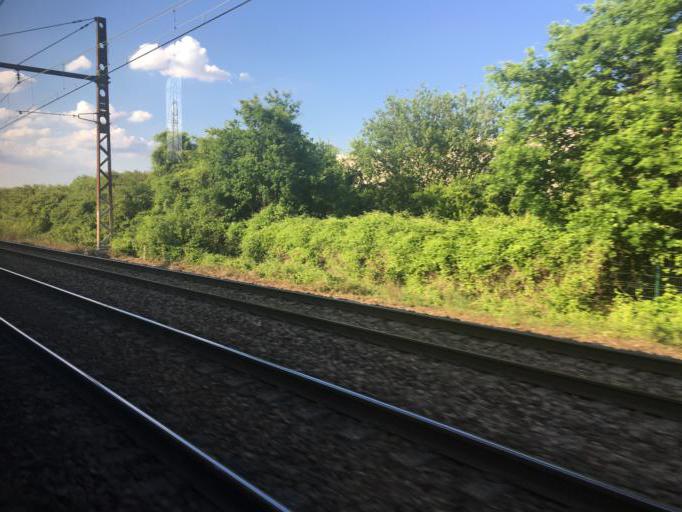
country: FR
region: Ile-de-France
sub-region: Departement de Seine-et-Marne
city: Moissy-Cramayel
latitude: 48.6174
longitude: 2.5743
